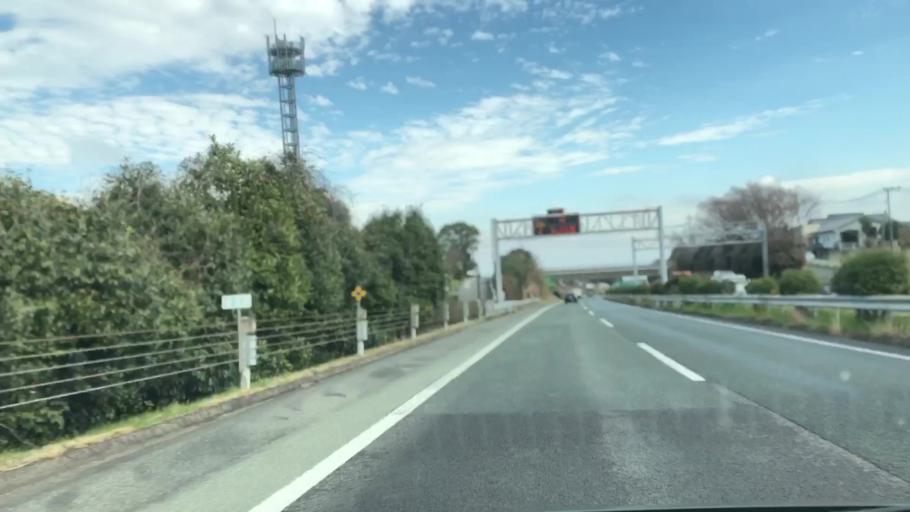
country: JP
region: Saga Prefecture
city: Tosu
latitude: 33.3970
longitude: 130.5108
